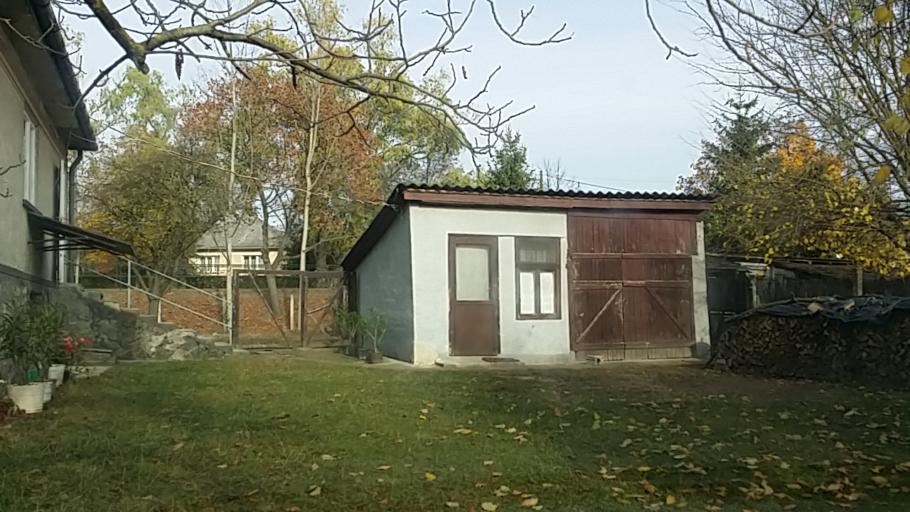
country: HU
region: Borsod-Abauj-Zemplen
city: Sarospatak
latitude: 48.4703
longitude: 21.5171
